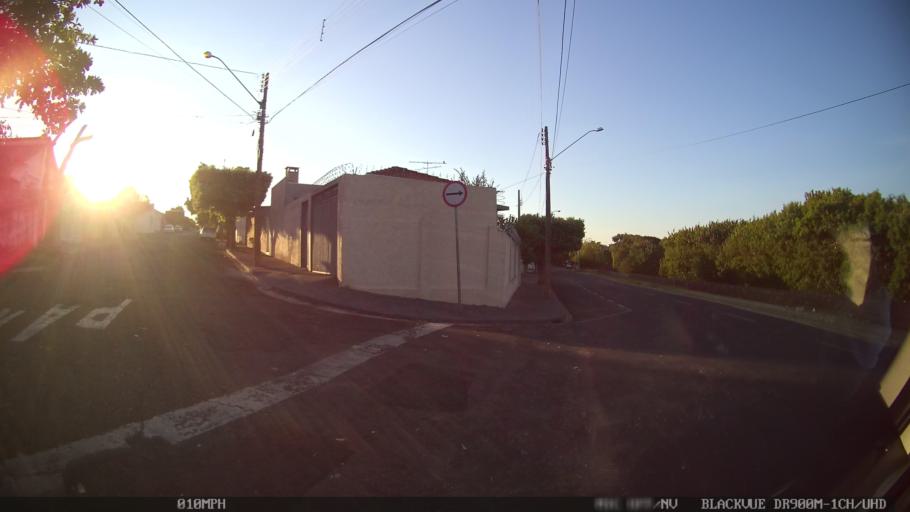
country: BR
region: Sao Paulo
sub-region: Sao Jose Do Rio Preto
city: Sao Jose do Rio Preto
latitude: -20.8020
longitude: -49.3793
